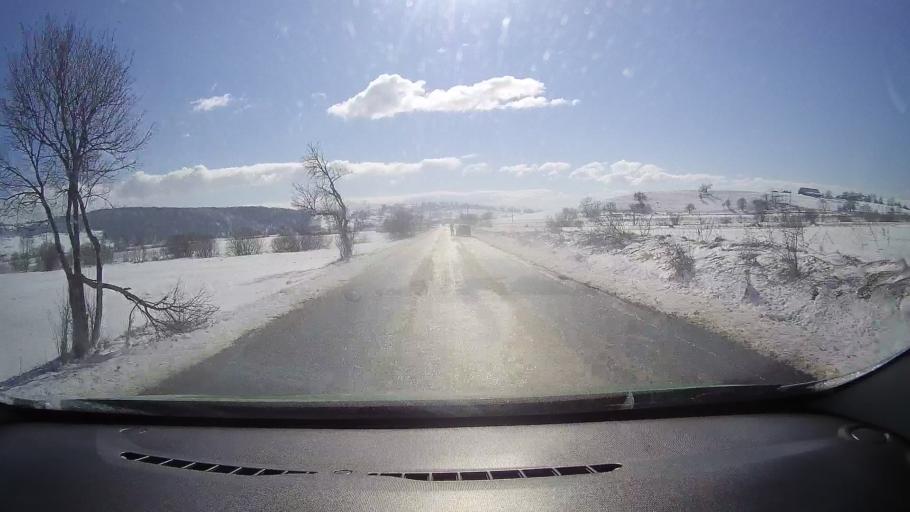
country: RO
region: Sibiu
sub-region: Comuna Vurpar
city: Vurpar
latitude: 45.8678
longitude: 24.3186
